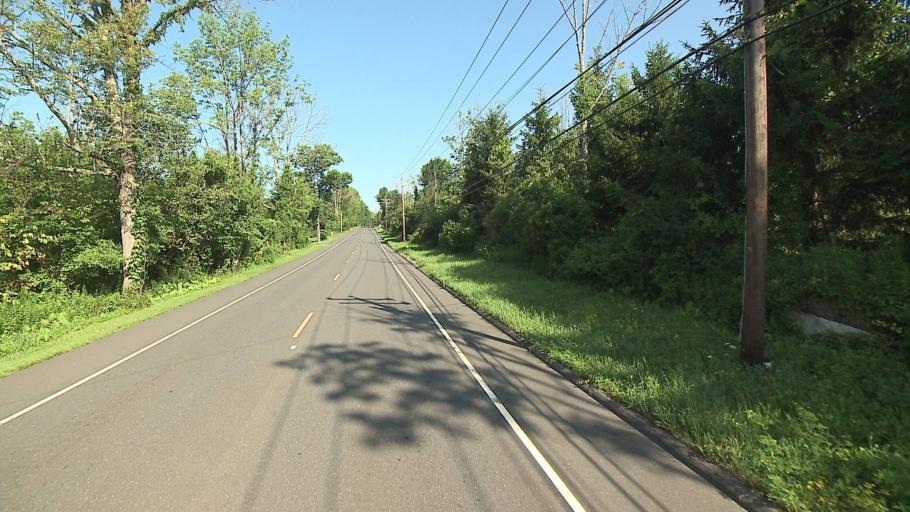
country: US
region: Connecticut
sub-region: Litchfield County
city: Litchfield
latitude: 41.8409
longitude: -73.2774
